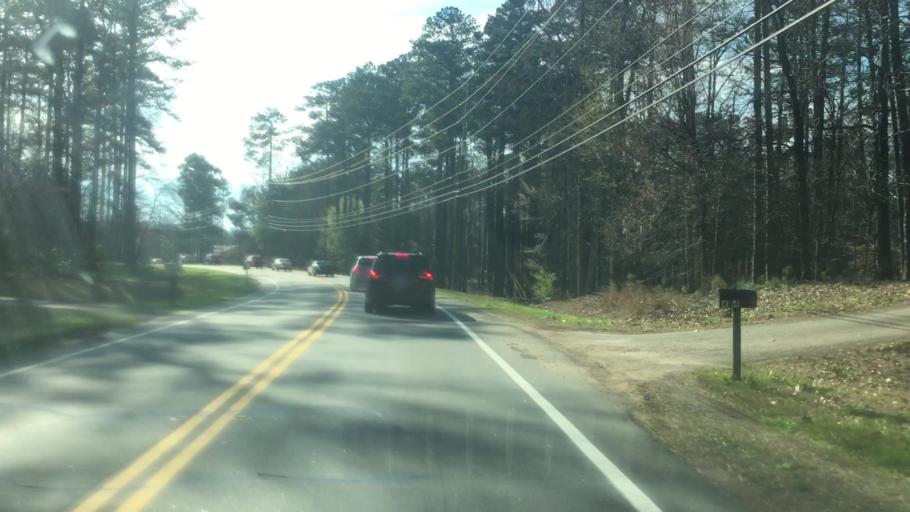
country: US
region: Georgia
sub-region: Cobb County
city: Kennesaw
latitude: 33.9994
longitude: -84.6718
